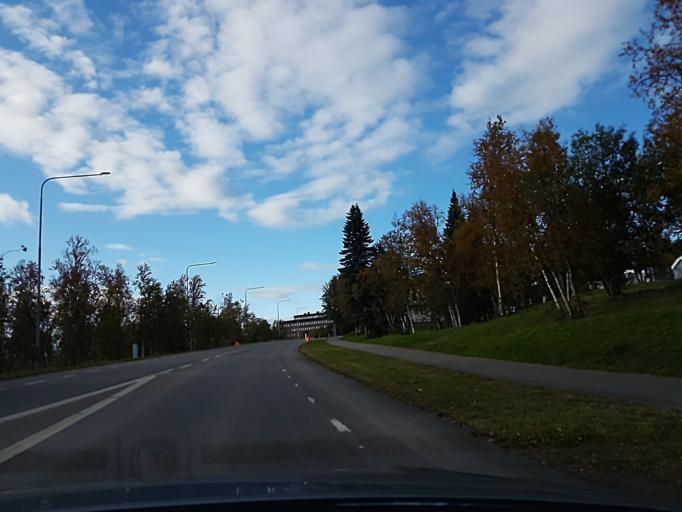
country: SE
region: Norrbotten
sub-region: Kiruna Kommun
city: Kiruna
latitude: 67.8493
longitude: 20.2261
